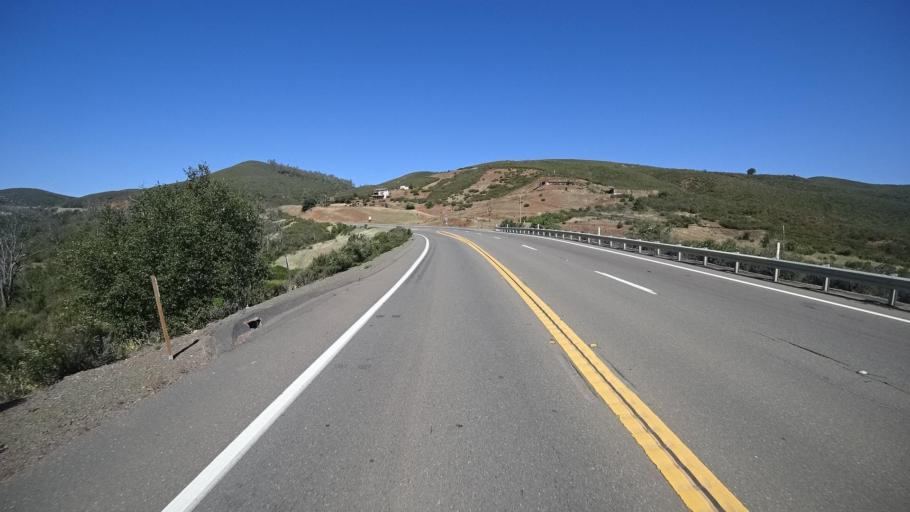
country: US
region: California
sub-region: Lake County
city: Clearlake
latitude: 39.0181
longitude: -122.5954
